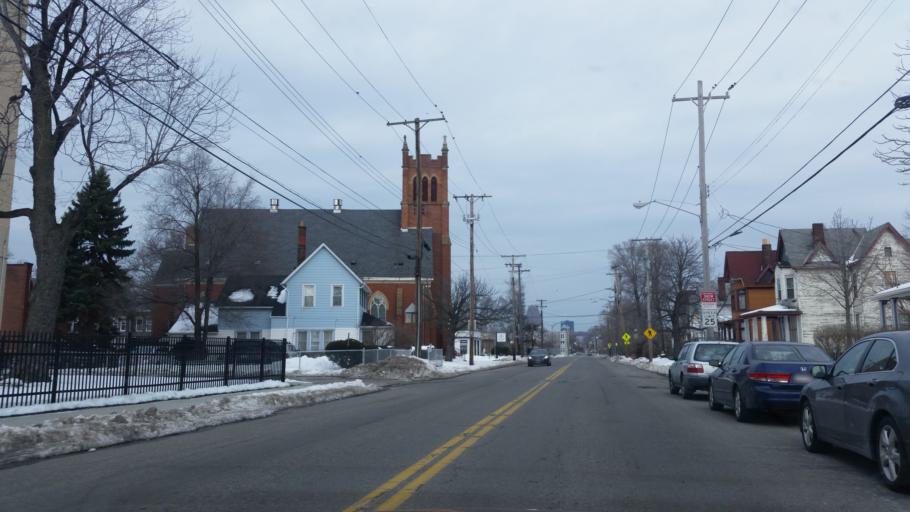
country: US
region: Ohio
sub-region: Cuyahoga County
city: Cleveland
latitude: 41.4718
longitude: -81.6964
